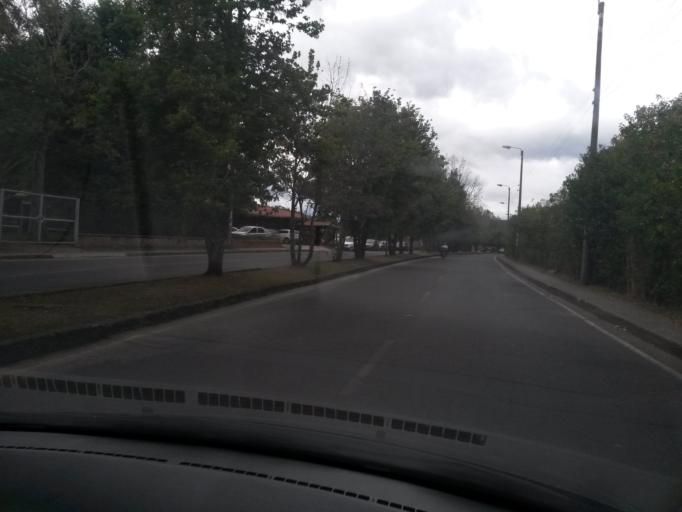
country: CO
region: Cauca
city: Popayan
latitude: 2.4600
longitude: -76.5989
